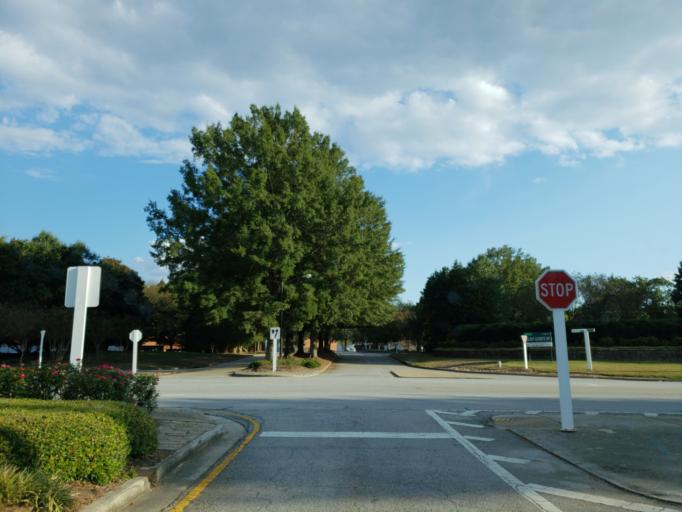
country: US
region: Georgia
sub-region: Cobb County
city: Mableton
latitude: 33.7635
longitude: -84.5623
